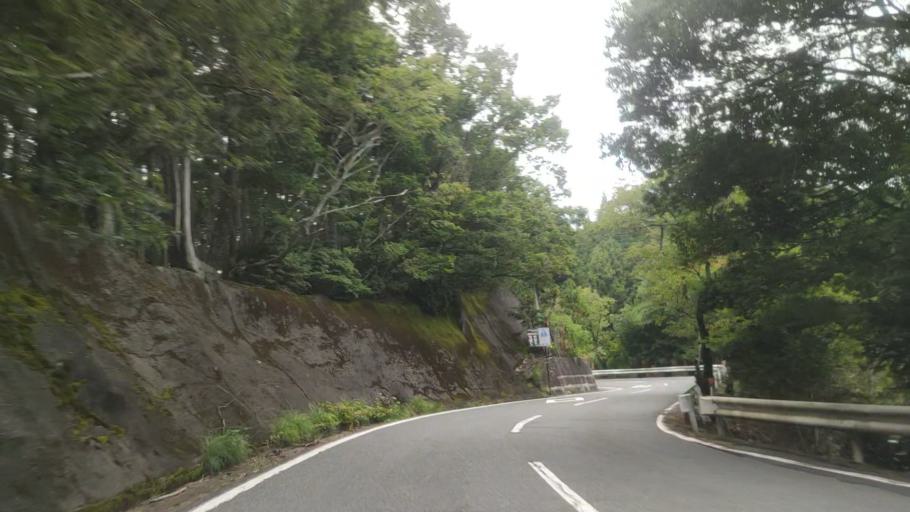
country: JP
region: Wakayama
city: Koya
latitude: 34.2163
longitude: 135.5497
